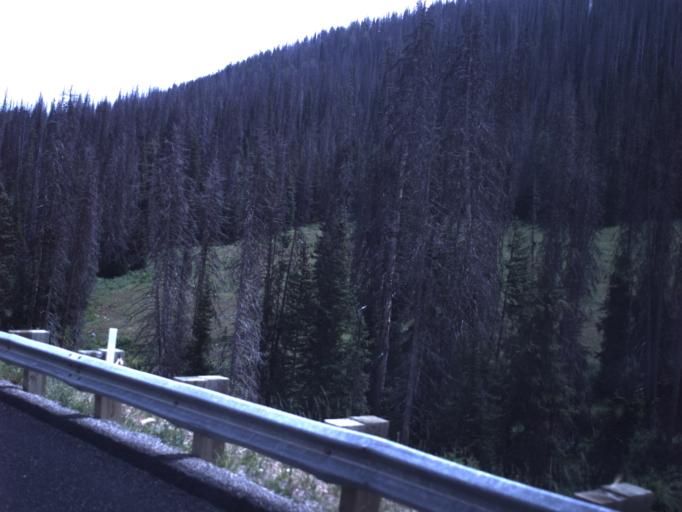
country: US
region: Utah
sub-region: Summit County
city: Francis
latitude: 40.4882
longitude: -110.9985
